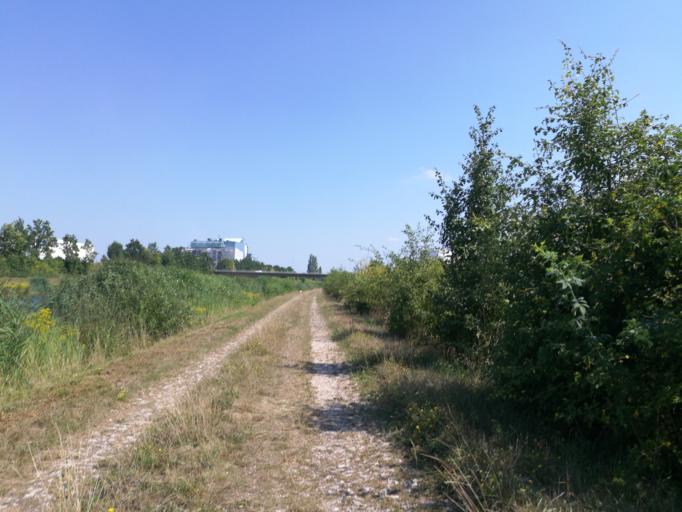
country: DE
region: Bavaria
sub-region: Regierungsbezirk Mittelfranken
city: Furth
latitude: 49.4943
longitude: 10.9453
